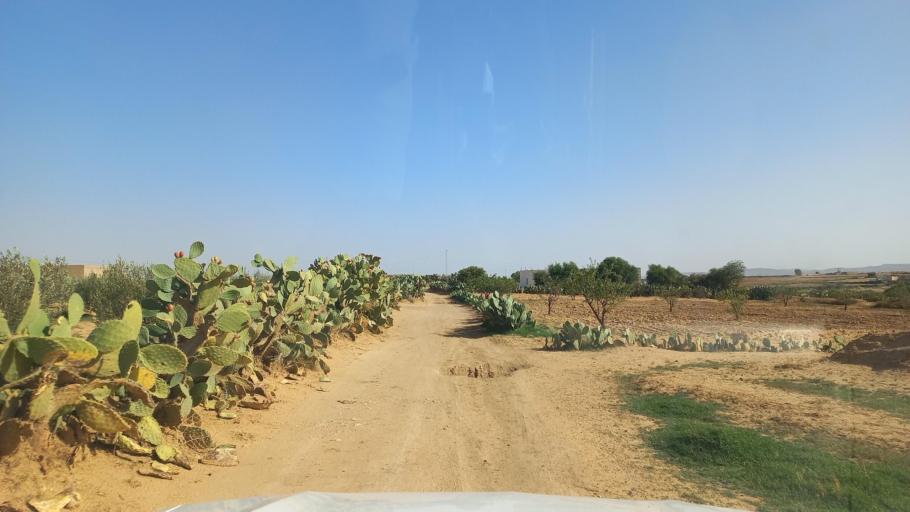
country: TN
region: Al Qasrayn
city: Sbiba
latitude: 35.3207
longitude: 9.0207
